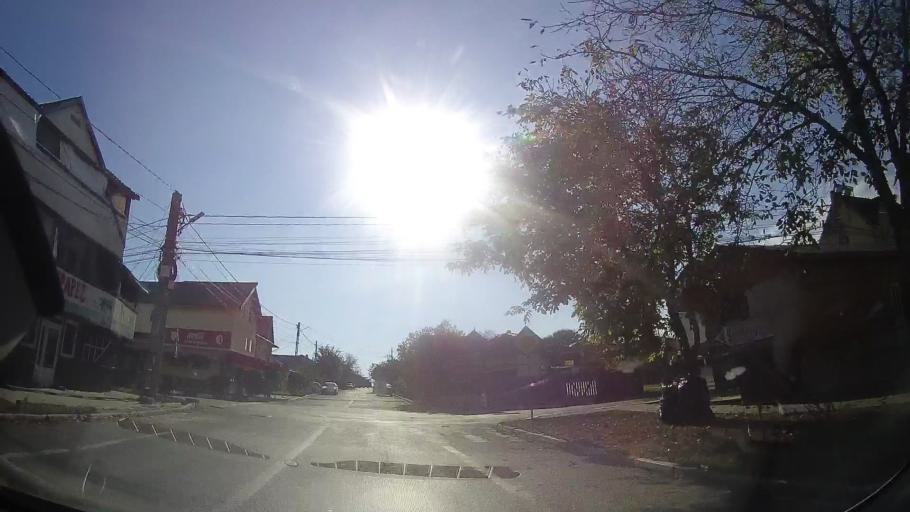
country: RO
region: Constanta
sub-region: Comuna Costinesti
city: Schitu
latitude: 43.9412
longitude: 28.6292
